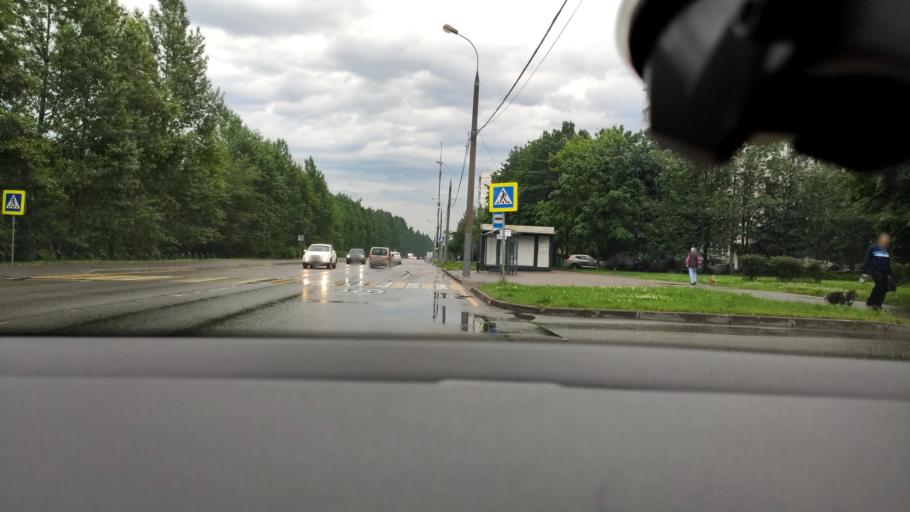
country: RU
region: Moscow
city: Yasenevo
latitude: 55.6156
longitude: 37.5520
